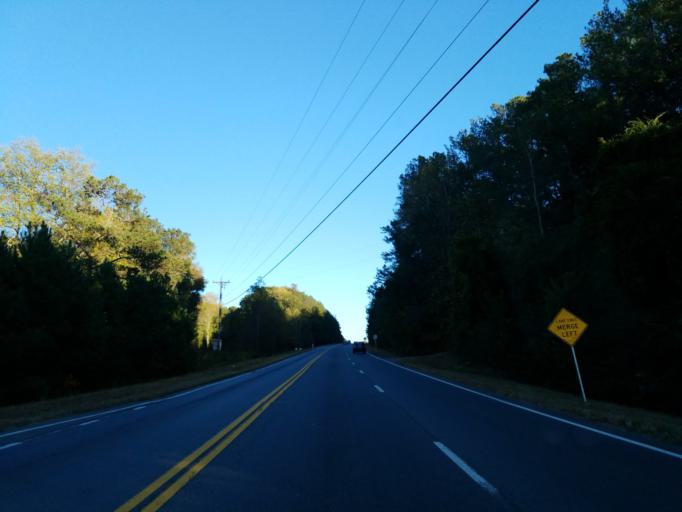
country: US
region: Georgia
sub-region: Dawson County
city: Dawsonville
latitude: 34.3808
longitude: -84.0594
